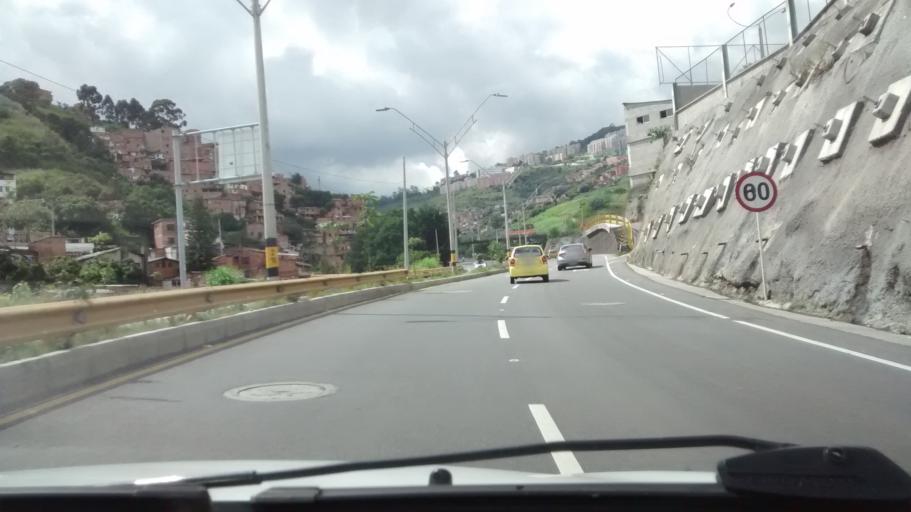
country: CO
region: Antioquia
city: Medellin
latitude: 6.2733
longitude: -75.5963
